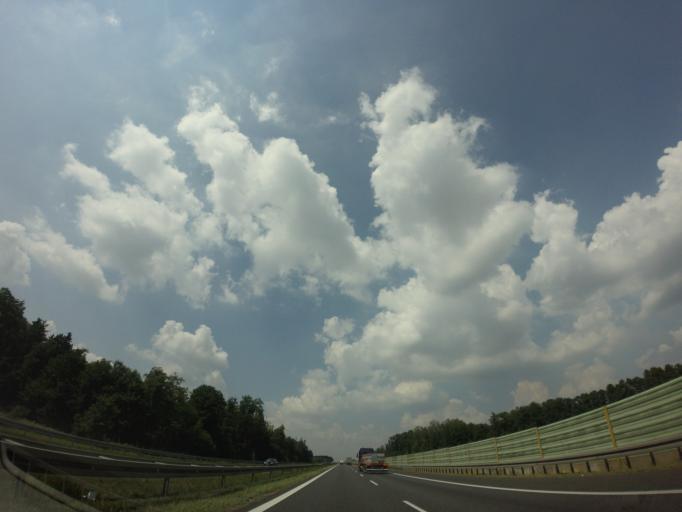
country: PL
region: Silesian Voivodeship
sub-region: Powiat gliwicki
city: Rudziniec
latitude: 50.3719
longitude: 18.4891
